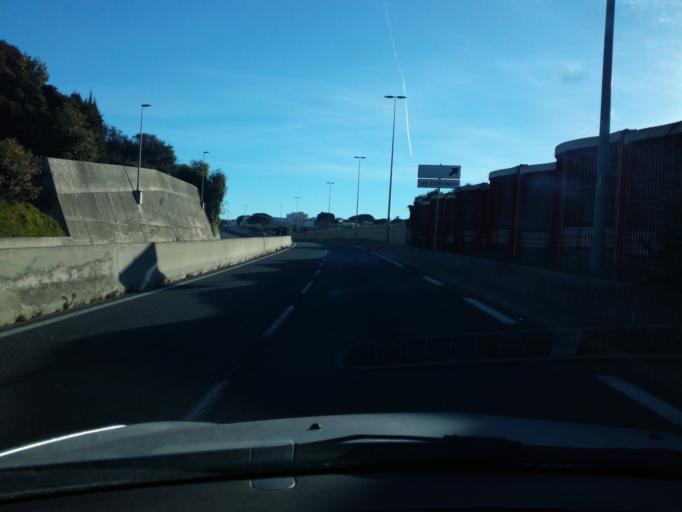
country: FR
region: Provence-Alpes-Cote d'Azur
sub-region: Departement des Alpes-Maritimes
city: Antibes
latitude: 43.5779
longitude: 7.1015
